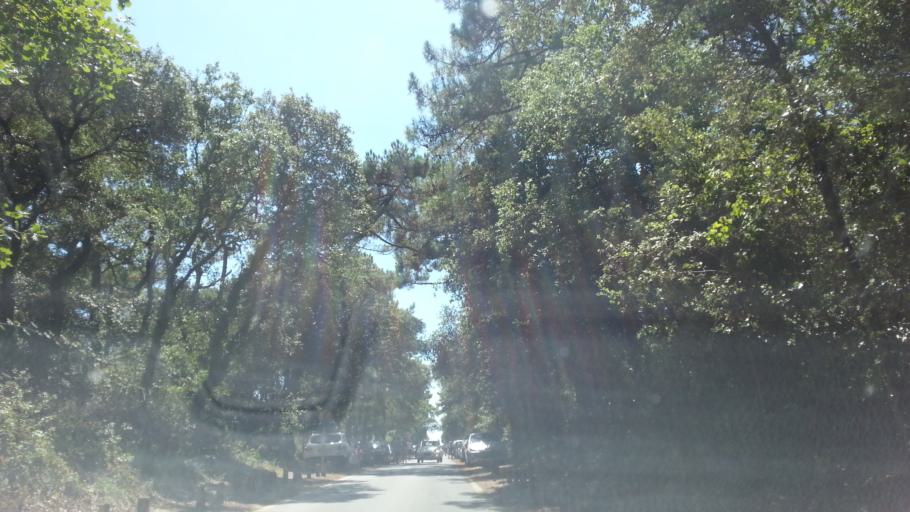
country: FR
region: Poitou-Charentes
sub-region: Departement de la Charente-Maritime
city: Dolus-d'Oleron
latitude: 45.8801
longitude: -1.2575
